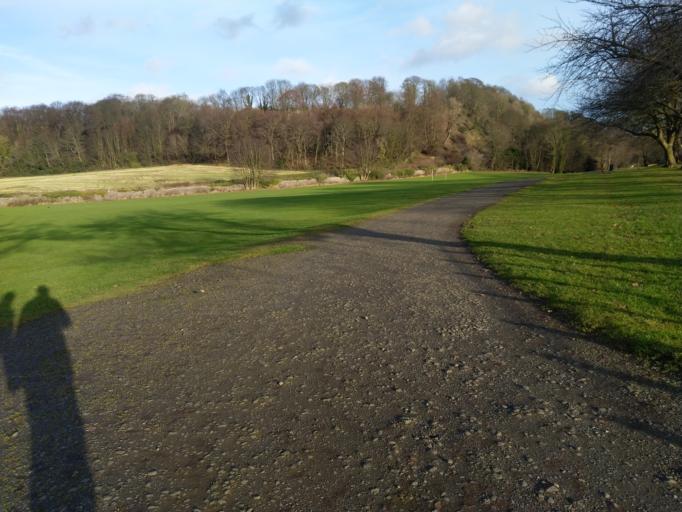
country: GB
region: Scotland
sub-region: Fife
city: Aberdour
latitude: 56.0551
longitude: -3.2910
